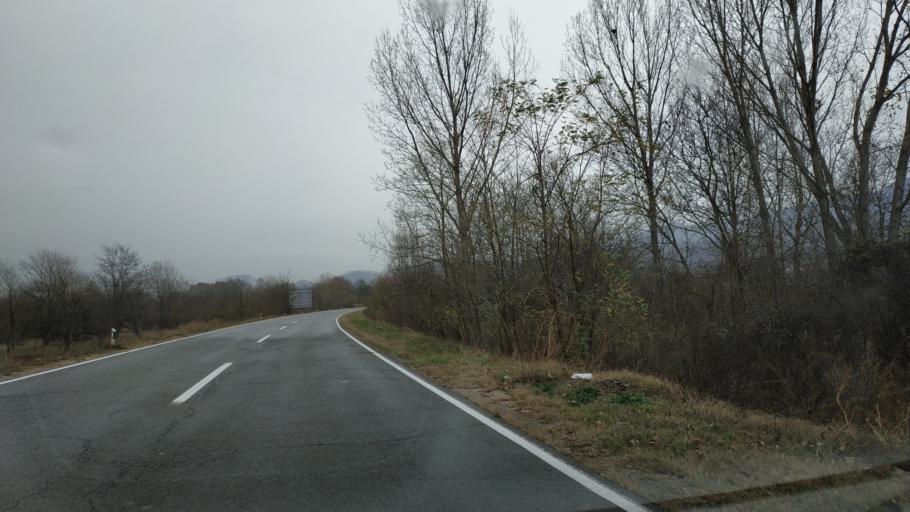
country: RS
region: Central Serbia
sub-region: Pirotski Okrug
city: Bela Palanka
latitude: 43.2305
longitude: 22.3228
